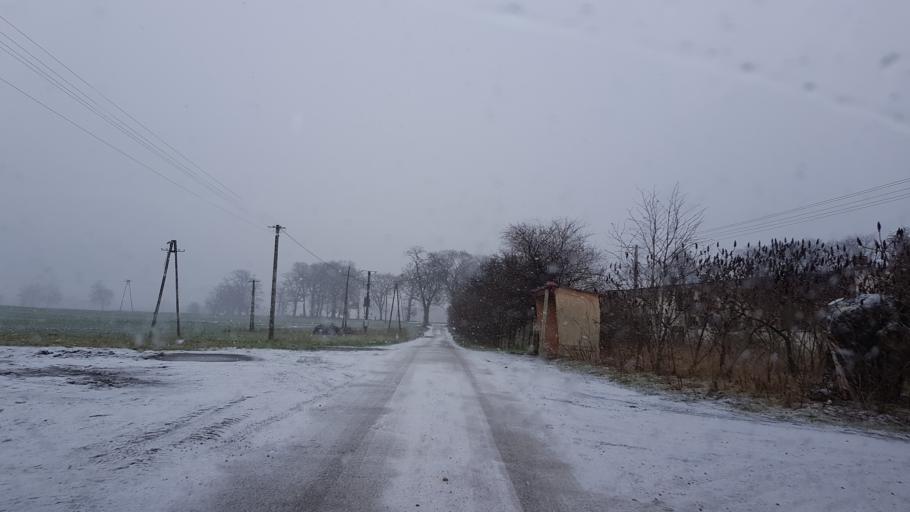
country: PL
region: West Pomeranian Voivodeship
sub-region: Powiat slawienski
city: Slawno
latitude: 54.2728
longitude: 16.6386
